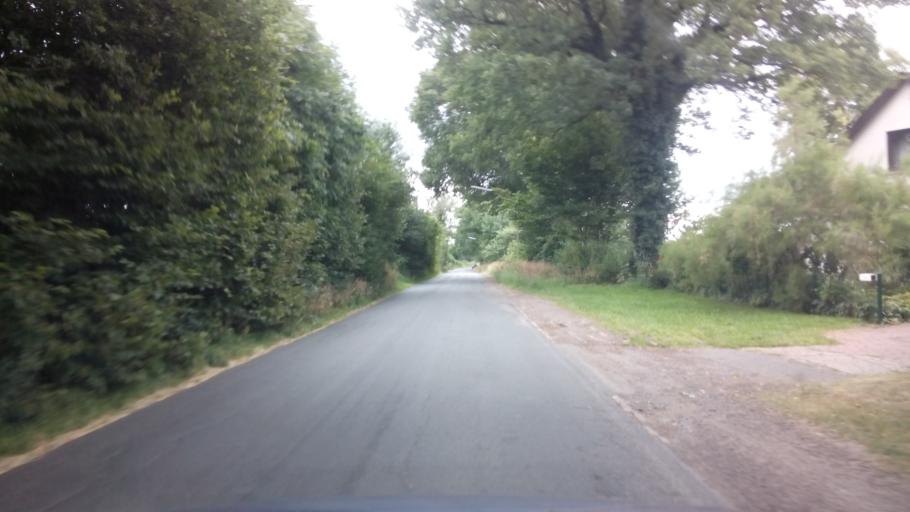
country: DE
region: Lower Saxony
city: Osterholz-Scharmbeck
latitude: 53.2220
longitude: 8.7538
